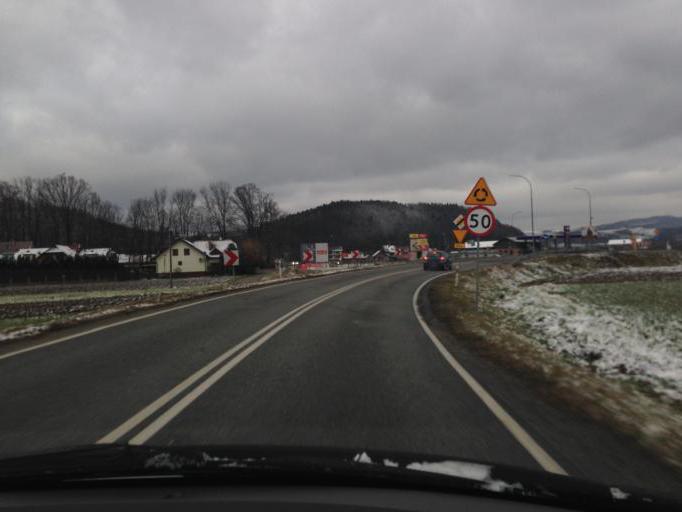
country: PL
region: Lesser Poland Voivodeship
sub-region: Powiat tarnowski
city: Zakliczyn
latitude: 49.8720
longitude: 20.8090
